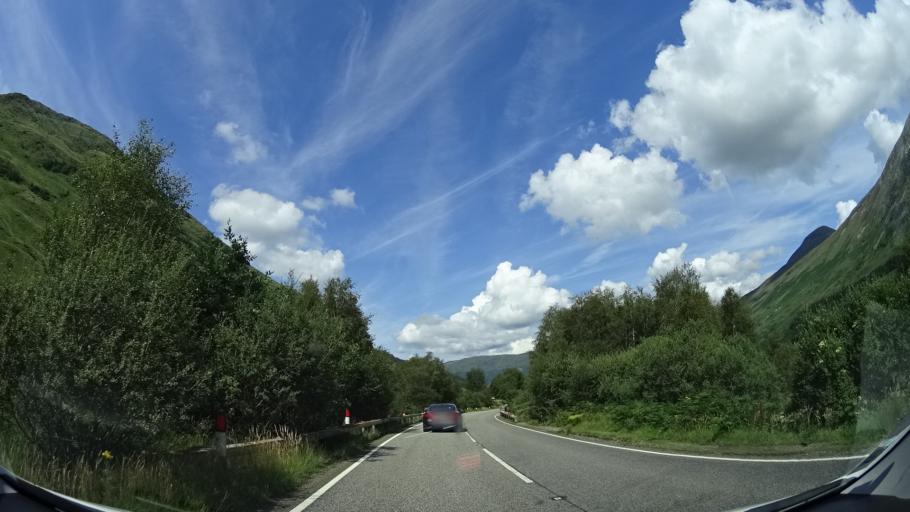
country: GB
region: Scotland
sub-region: Highland
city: Fort William
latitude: 56.6613
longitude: -5.0698
